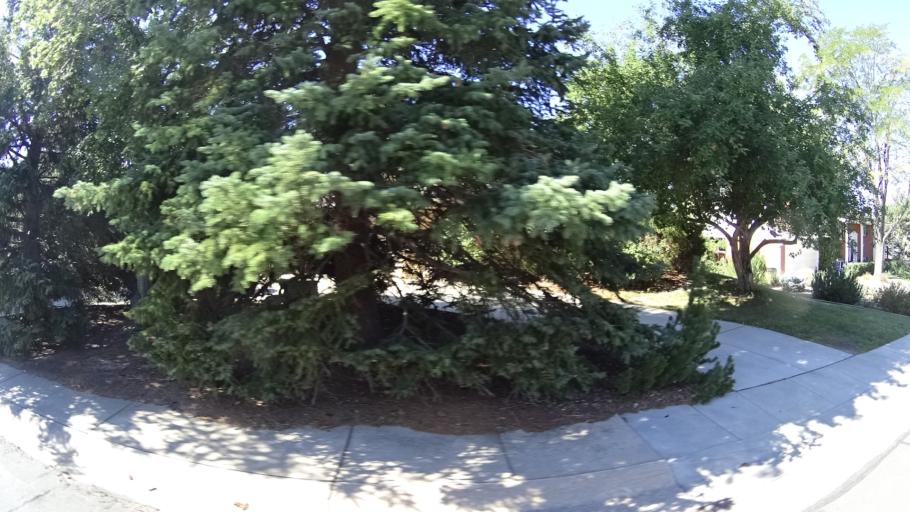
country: US
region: Colorado
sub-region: El Paso County
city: Colorado Springs
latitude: 38.8741
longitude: -104.7829
